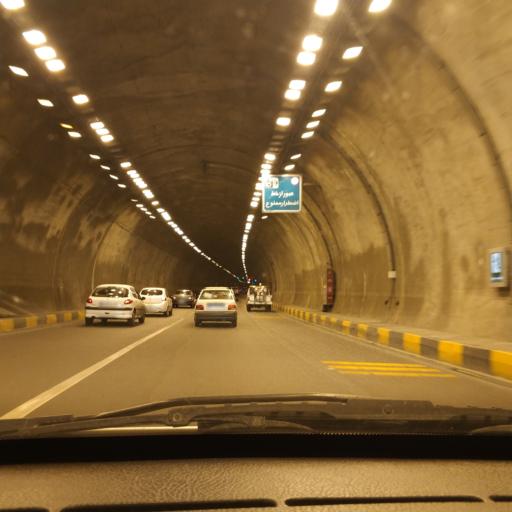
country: IR
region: Tehran
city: Tajrish
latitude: 35.7799
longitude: 51.4309
